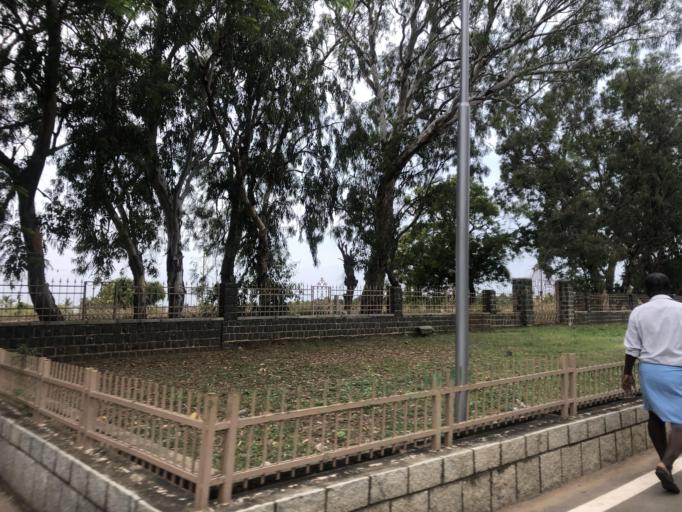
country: IN
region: Tamil Nadu
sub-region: Kancheepuram
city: Mamallapuram
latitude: 12.6107
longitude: 80.1902
